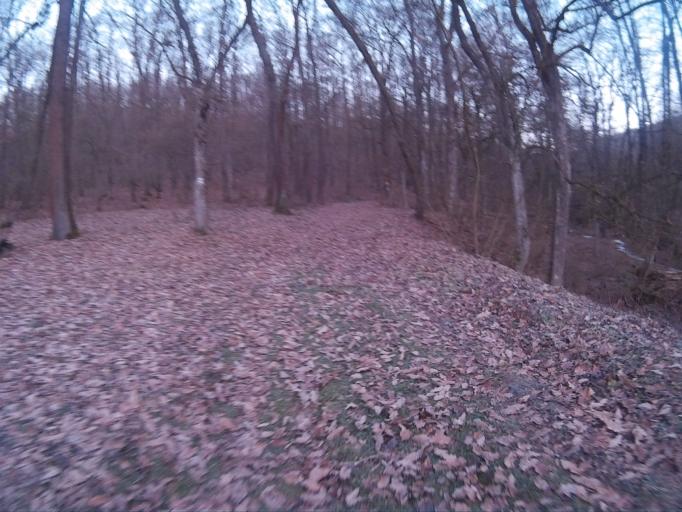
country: HU
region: Borsod-Abauj-Zemplen
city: Putnok
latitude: 48.3169
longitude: 20.4403
